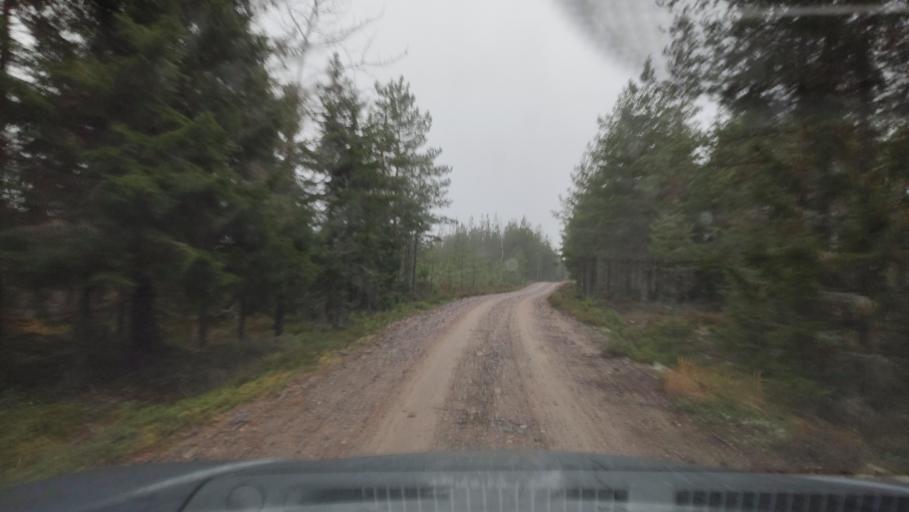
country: FI
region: Southern Ostrobothnia
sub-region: Suupohja
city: Karijoki
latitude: 62.1891
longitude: 21.7428
